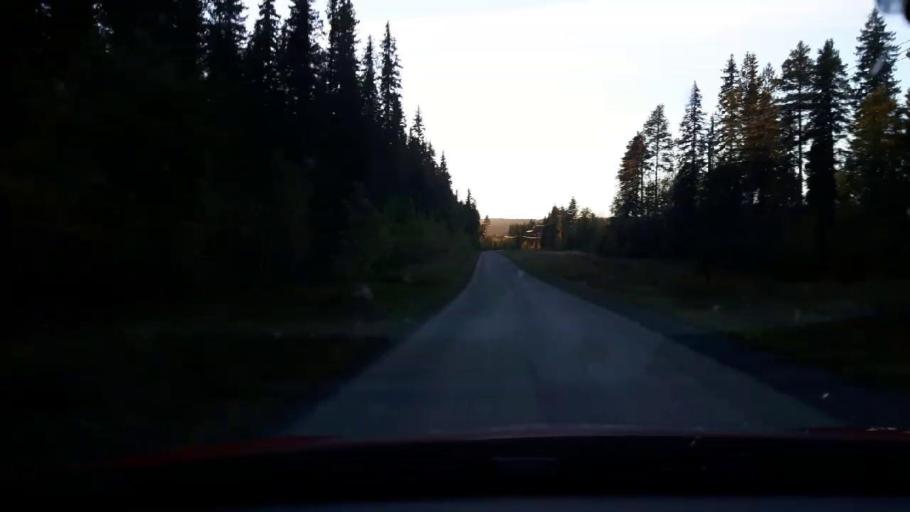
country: SE
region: Jaemtland
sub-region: Krokoms Kommun
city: Krokom
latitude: 63.4768
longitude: 14.2544
